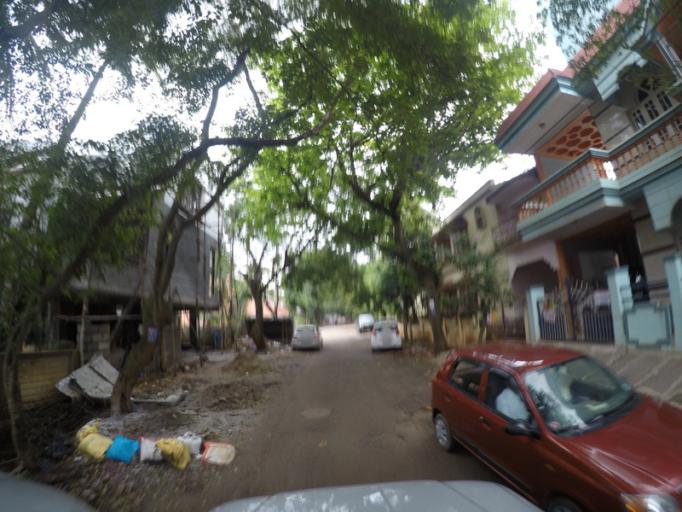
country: IN
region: Karnataka
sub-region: Bangalore Urban
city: Yelahanka
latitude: 13.0791
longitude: 77.5572
